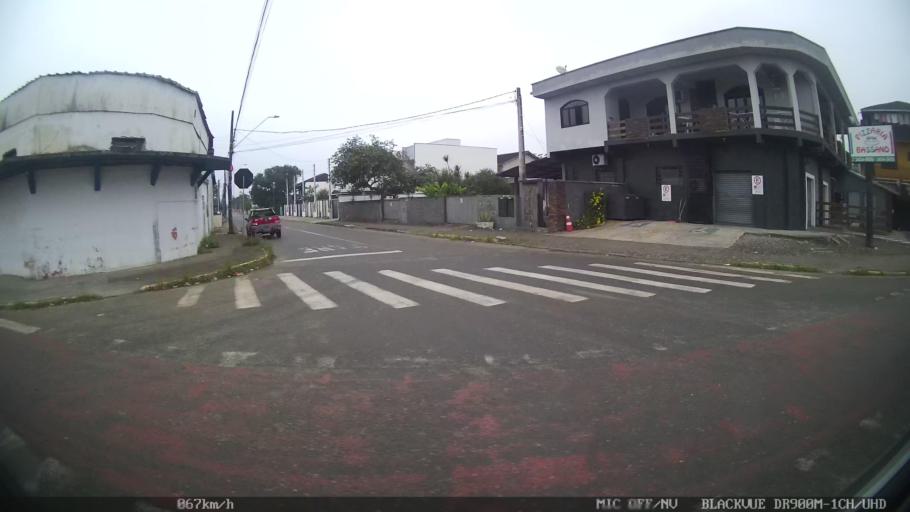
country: BR
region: Santa Catarina
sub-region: Joinville
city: Joinville
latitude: -26.2841
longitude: -48.8059
